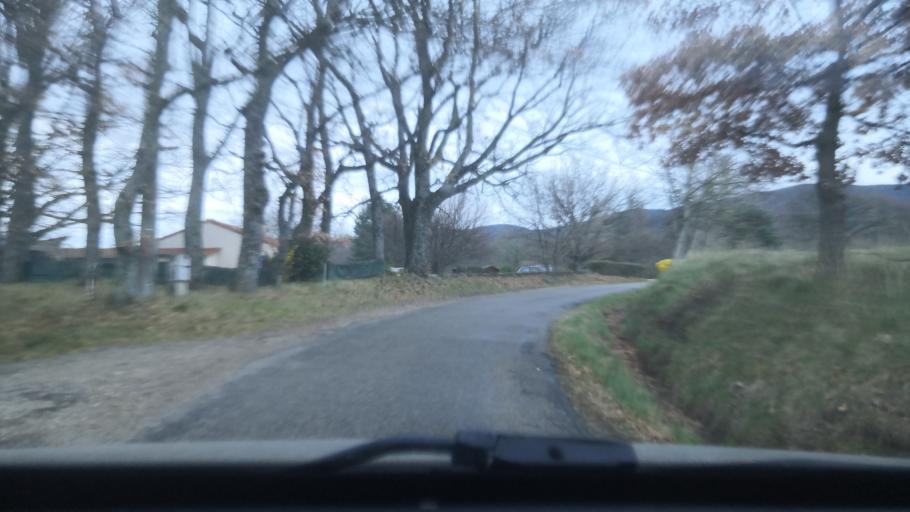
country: FR
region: Rhone-Alpes
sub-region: Departement de la Drome
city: Dieulefit
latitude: 44.5237
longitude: 5.0223
